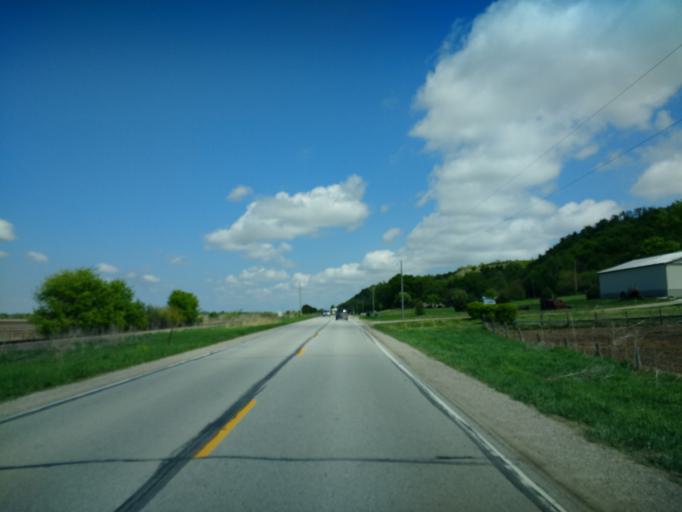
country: US
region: Iowa
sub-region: Harrison County
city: Missouri Valley
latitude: 41.4754
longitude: -95.8820
